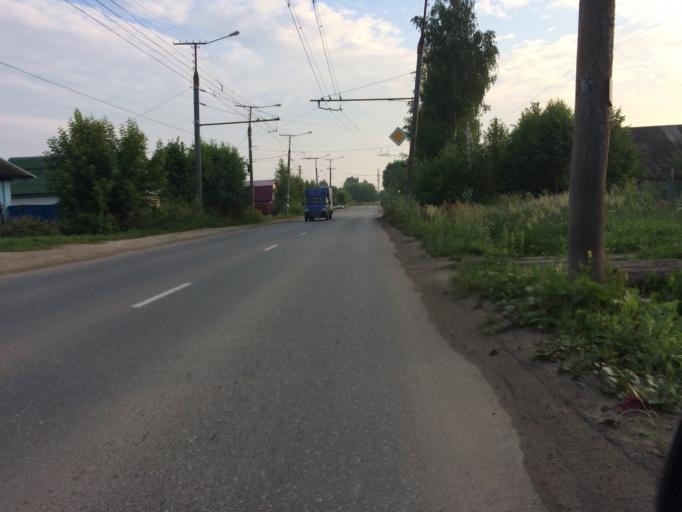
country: RU
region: Mariy-El
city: Yoshkar-Ola
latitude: 56.6452
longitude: 47.9543
